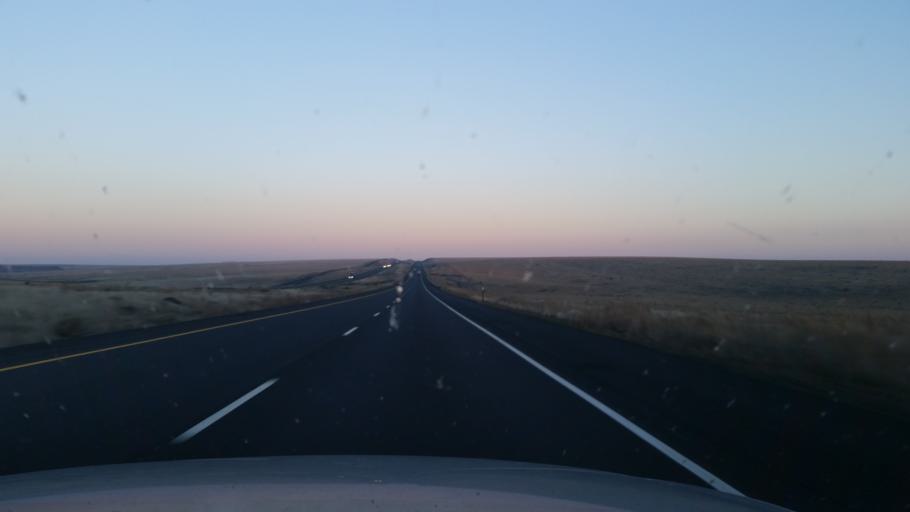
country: US
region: Washington
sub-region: Grant County
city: Warden
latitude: 47.0860
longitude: -118.7600
